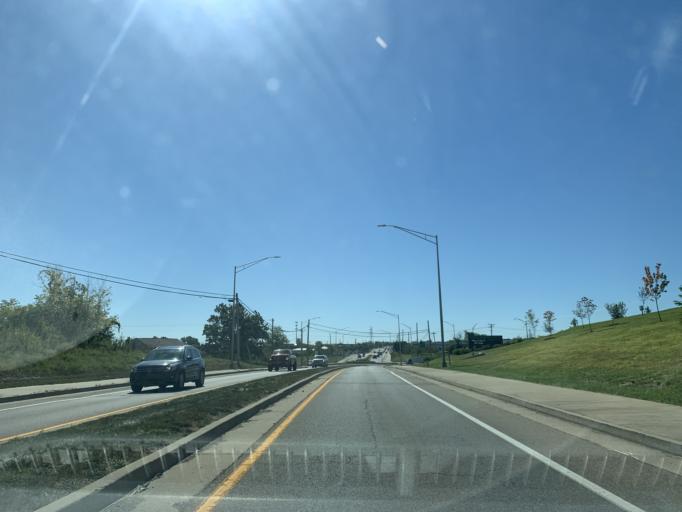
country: US
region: Kentucky
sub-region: Boone County
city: Francisville
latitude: 39.0944
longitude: -84.7148
